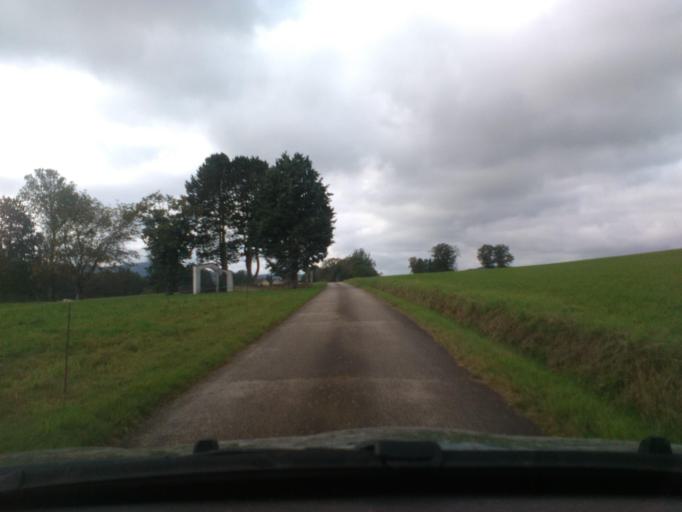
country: FR
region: Lorraine
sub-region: Departement des Vosges
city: Etival-Clairefontaine
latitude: 48.3366
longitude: 6.8586
